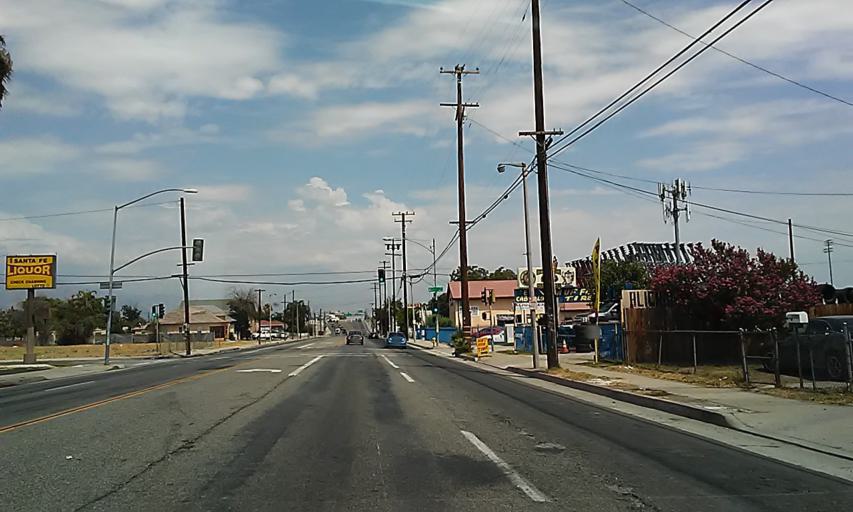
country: US
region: California
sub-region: San Bernardino County
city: San Bernardino
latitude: 34.1083
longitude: -117.3096
